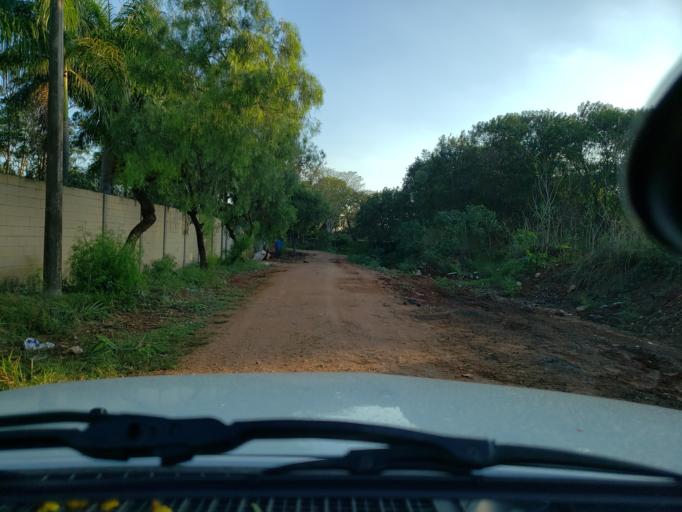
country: BR
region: Sao Paulo
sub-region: Moji-Guacu
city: Mogi-Gaucu
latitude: -22.3387
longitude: -46.9384
